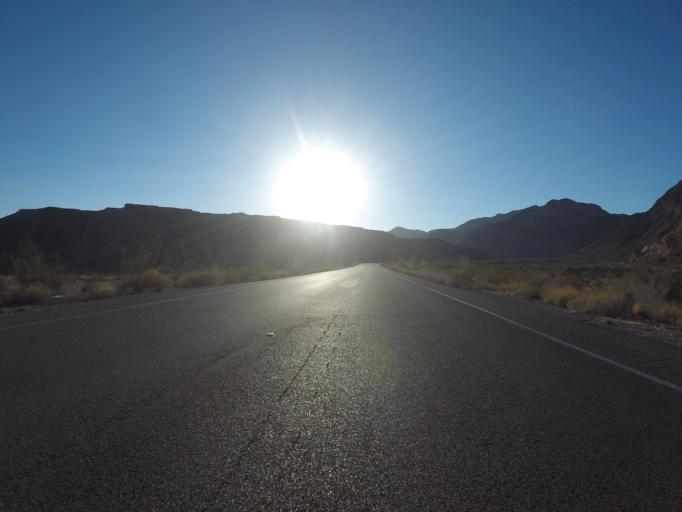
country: US
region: Nevada
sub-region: Clark County
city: Moapa Valley
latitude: 36.3635
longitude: -114.4674
